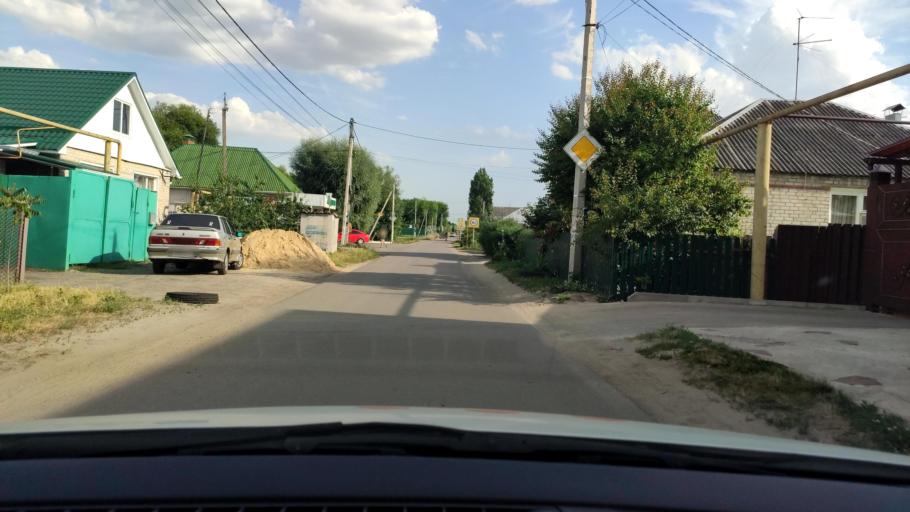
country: RU
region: Voronezj
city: Novaya Usman'
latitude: 51.6353
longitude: 39.4136
